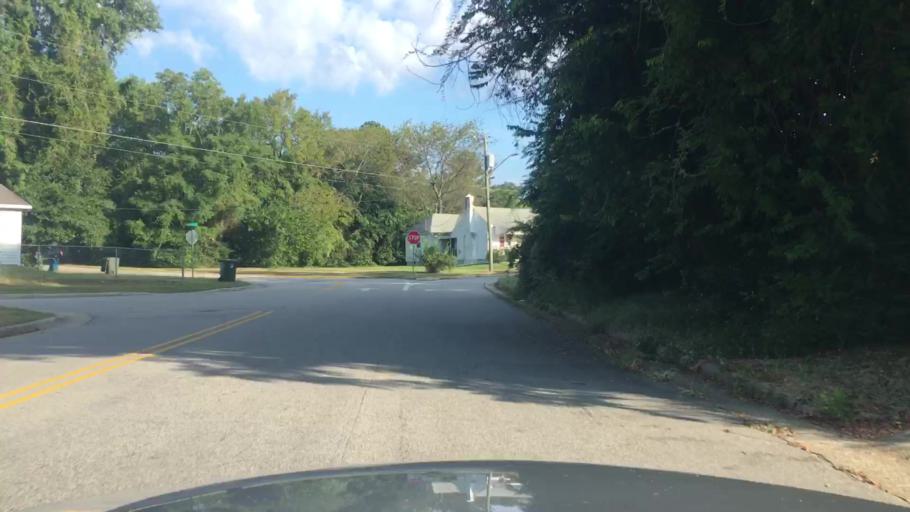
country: US
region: North Carolina
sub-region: Cumberland County
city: Fayetteville
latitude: 35.0481
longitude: -78.8913
